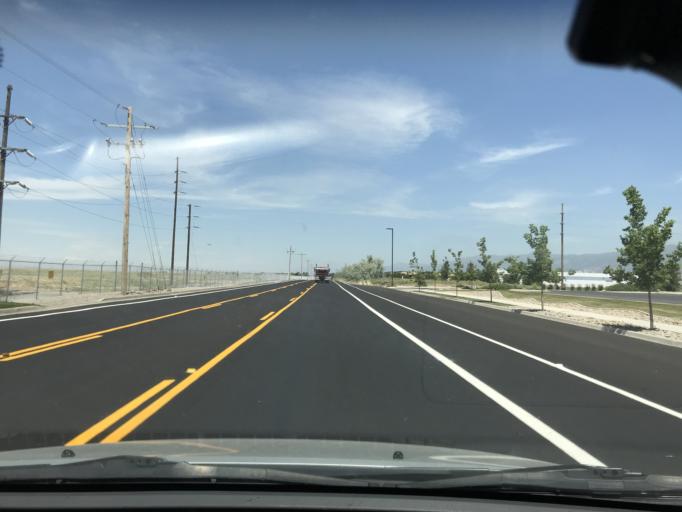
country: US
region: Utah
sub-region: Davis County
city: North Salt Lake
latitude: 40.7975
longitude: -111.9535
